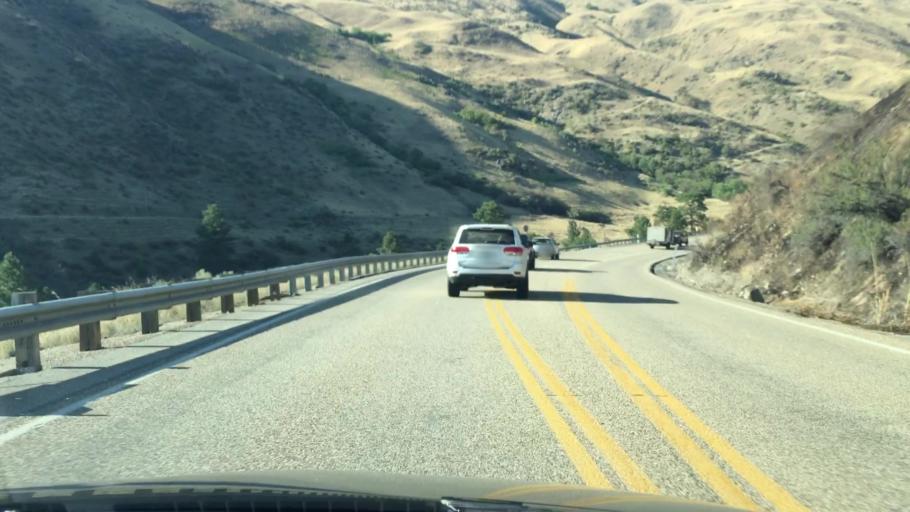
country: US
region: Idaho
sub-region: Gem County
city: Emmett
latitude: 44.0039
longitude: -116.1803
